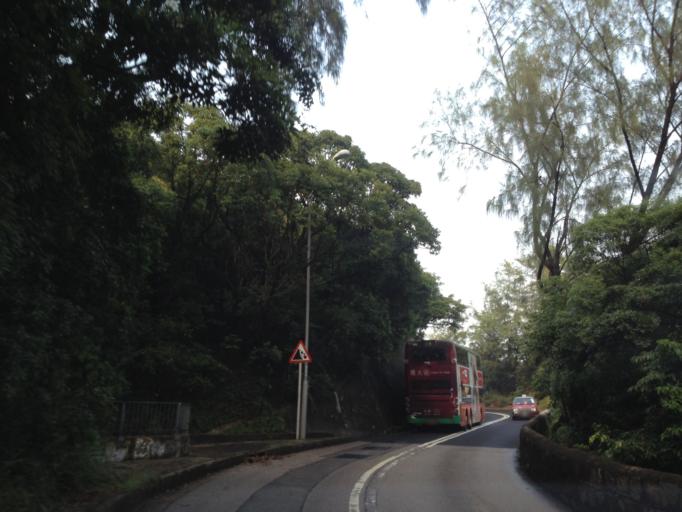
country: HK
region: Wanchai
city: Wan Chai
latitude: 22.2536
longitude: 114.2270
